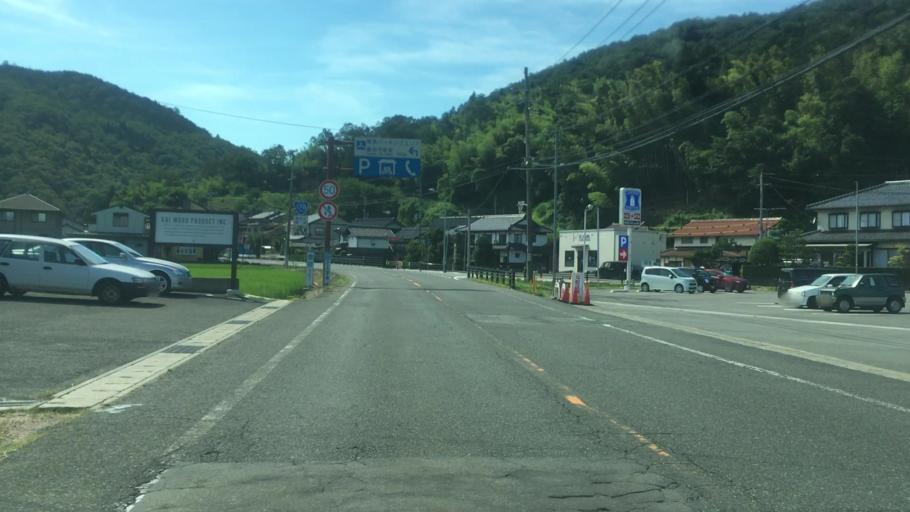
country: JP
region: Hyogo
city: Toyooka
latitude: 35.5666
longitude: 134.7882
